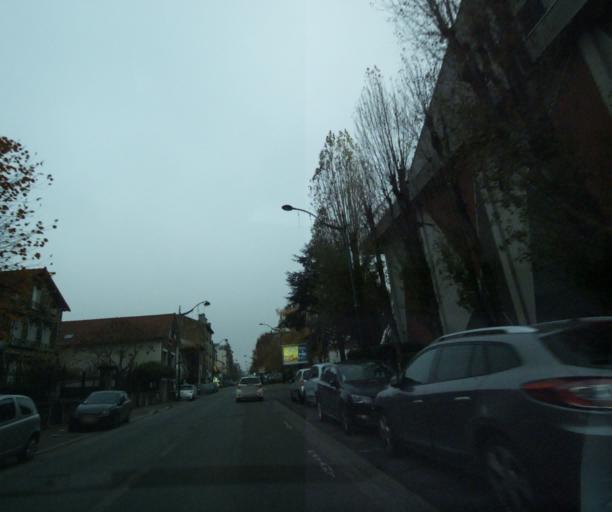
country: FR
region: Ile-de-France
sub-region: Departement de Seine-Saint-Denis
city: Les Pavillons-sous-Bois
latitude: 48.9034
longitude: 2.5070
